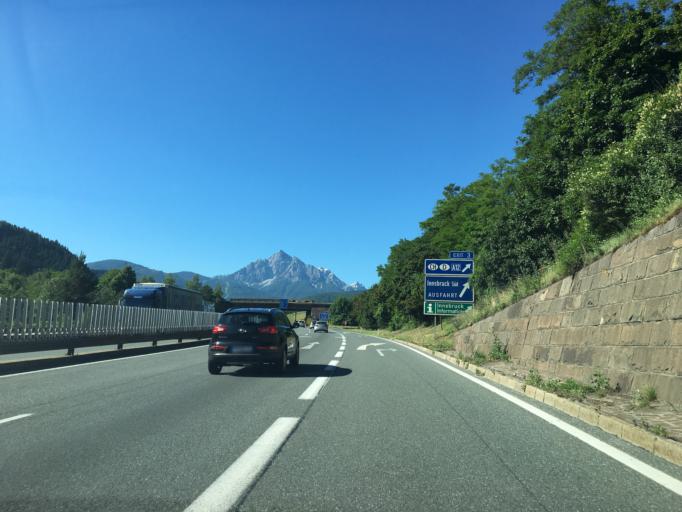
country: AT
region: Tyrol
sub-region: Politischer Bezirk Innsbruck Land
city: Mutters
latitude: 47.2419
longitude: 11.3904
